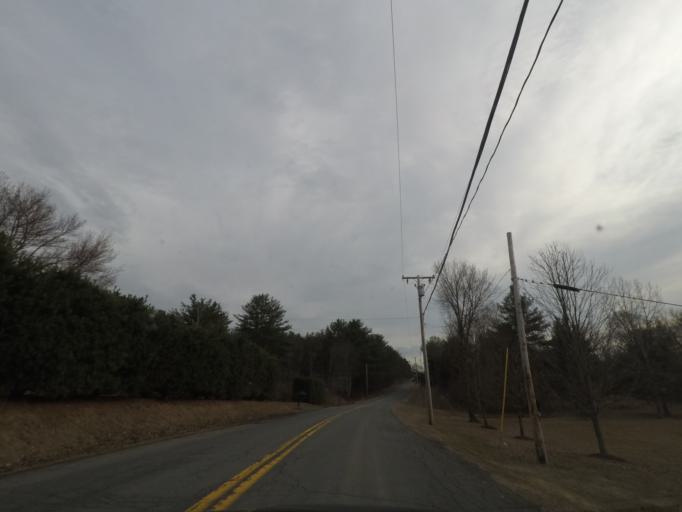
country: US
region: New York
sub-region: Rensselaer County
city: Hoosick Falls
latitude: 42.8487
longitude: -73.4555
